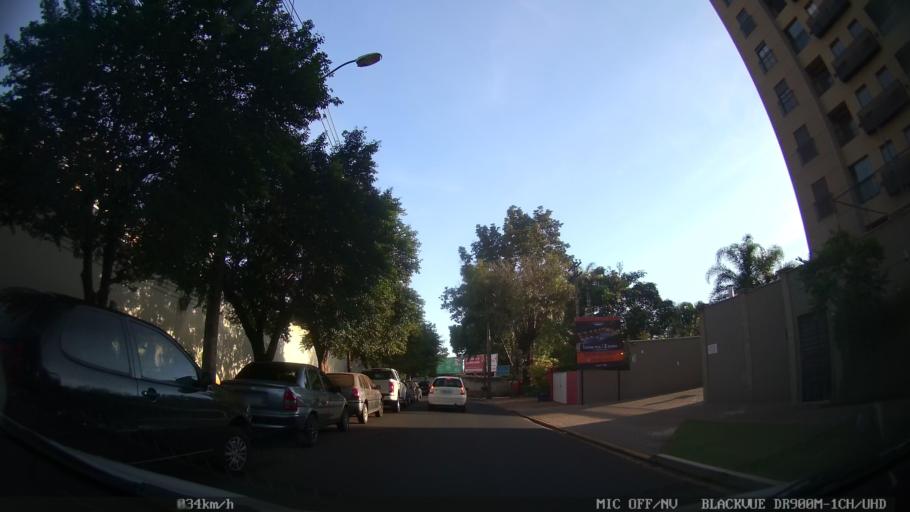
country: BR
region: Sao Paulo
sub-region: Ribeirao Preto
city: Ribeirao Preto
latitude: -21.2064
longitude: -47.7932
